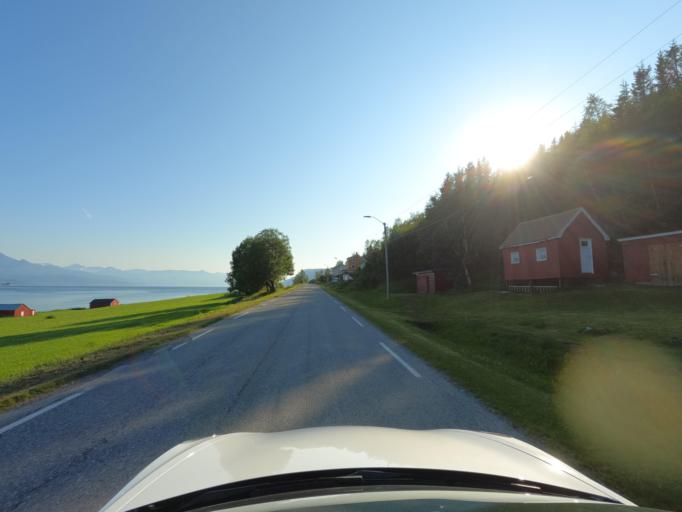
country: NO
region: Nordland
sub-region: Narvik
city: Narvik
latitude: 68.5280
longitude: 17.4587
